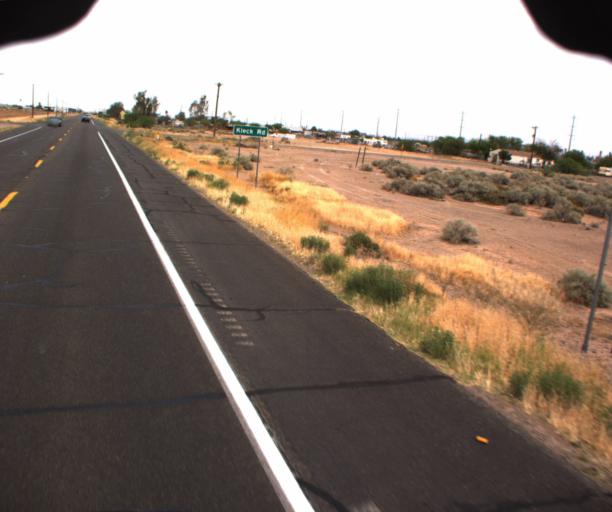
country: US
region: Arizona
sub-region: Pinal County
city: Coolidge
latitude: 32.9075
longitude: -111.5151
